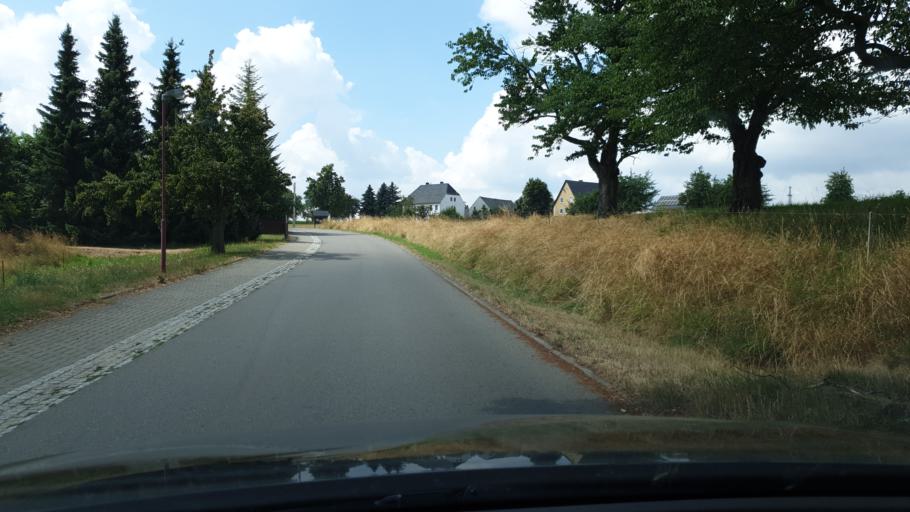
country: DE
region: Saxony
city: Erlau
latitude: 51.0417
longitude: 12.9714
